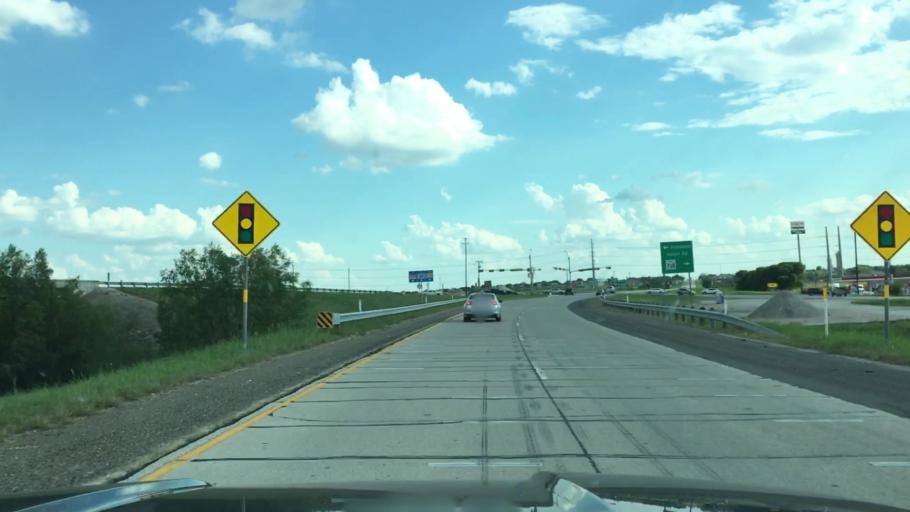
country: US
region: Texas
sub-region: Tarrant County
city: Pecan Acres
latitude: 32.9699
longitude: -97.4207
